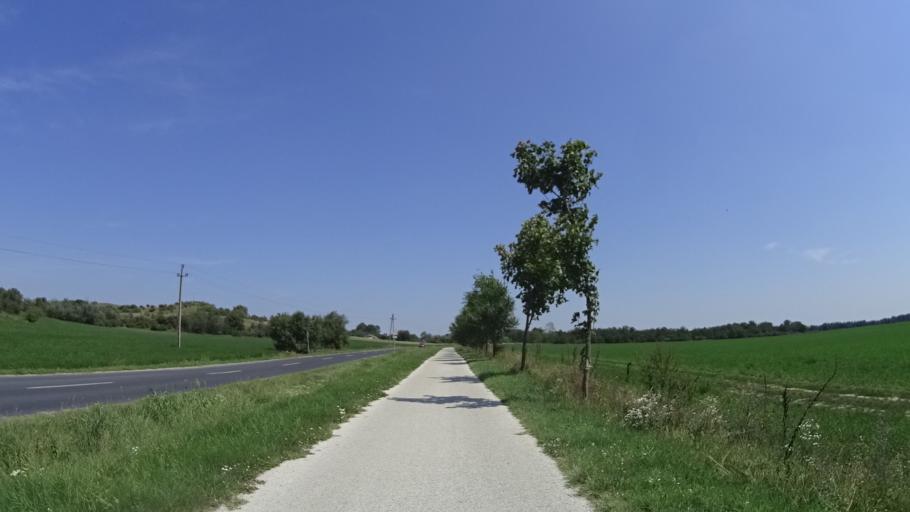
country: HU
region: Fejer
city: Pakozd
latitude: 47.2099
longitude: 18.5140
